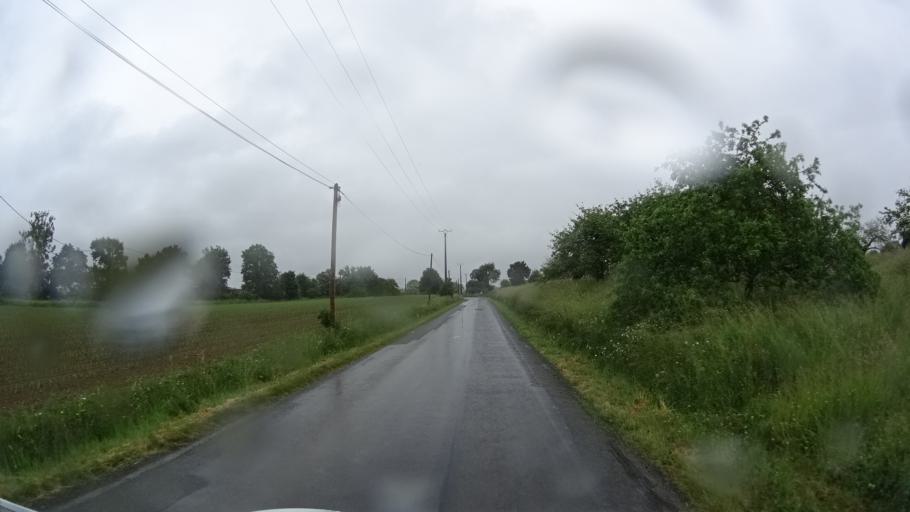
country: FR
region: Brittany
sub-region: Departement d'Ille-et-Vilaine
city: Saint-Erblon
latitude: 48.0290
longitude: -1.6375
